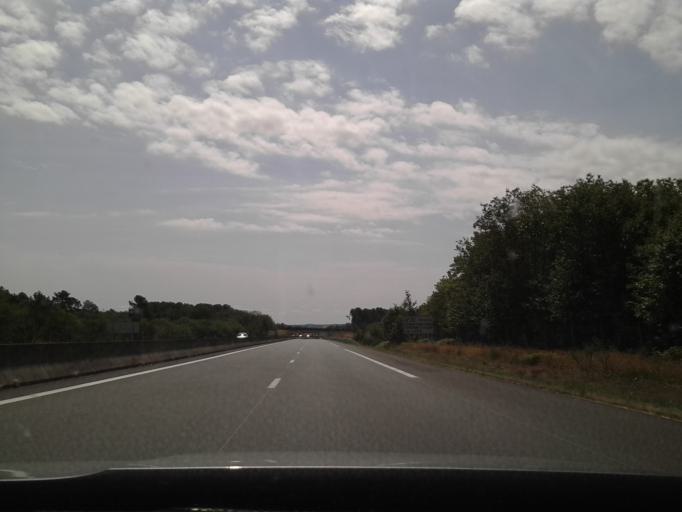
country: FR
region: Pays de la Loire
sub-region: Departement de la Sarthe
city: Luceau
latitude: 47.7014
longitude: 0.3535
